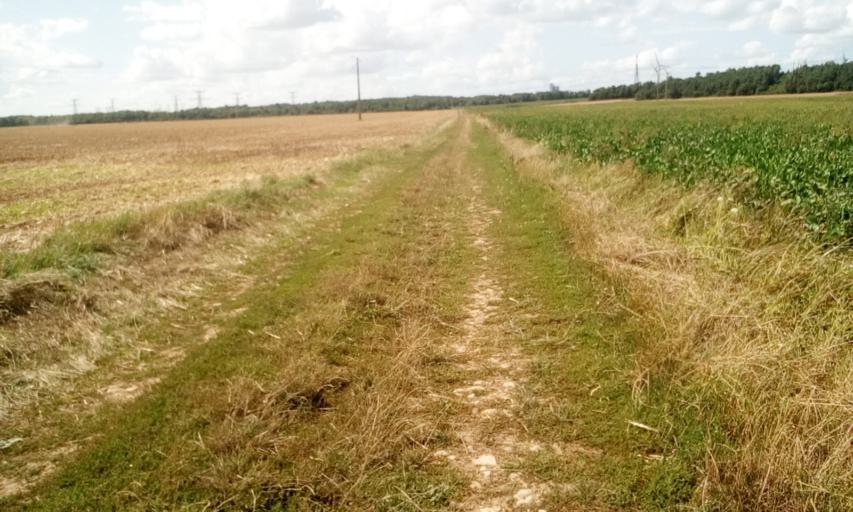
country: FR
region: Lower Normandy
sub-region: Departement du Calvados
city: Bellengreville
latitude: 49.1100
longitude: -0.2319
